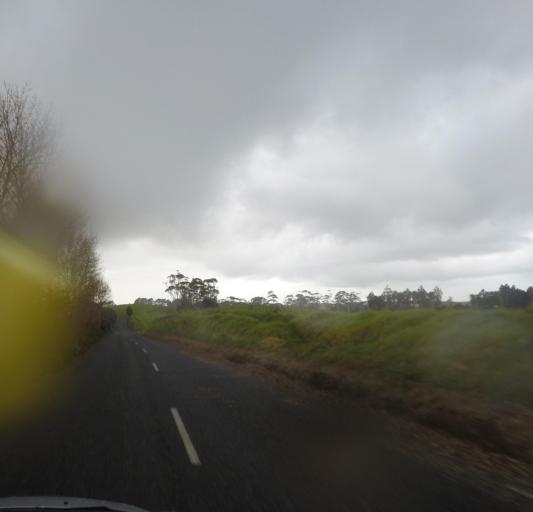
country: NZ
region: Auckland
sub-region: Auckland
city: Warkworth
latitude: -36.3737
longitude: 174.7623
